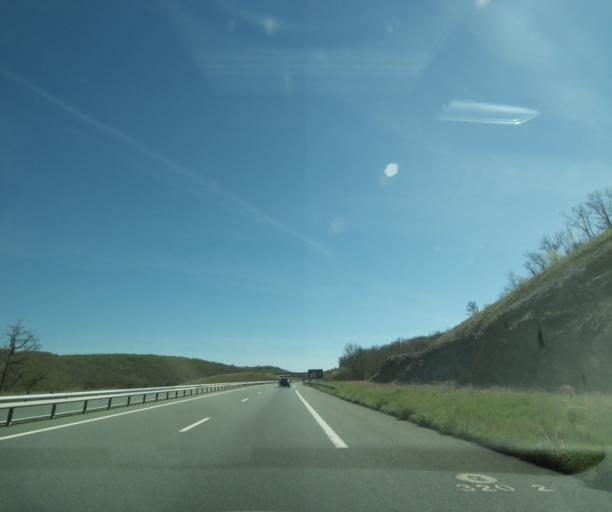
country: FR
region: Midi-Pyrenees
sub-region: Departement du Lot
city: Le Vigan
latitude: 44.7767
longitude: 1.5348
